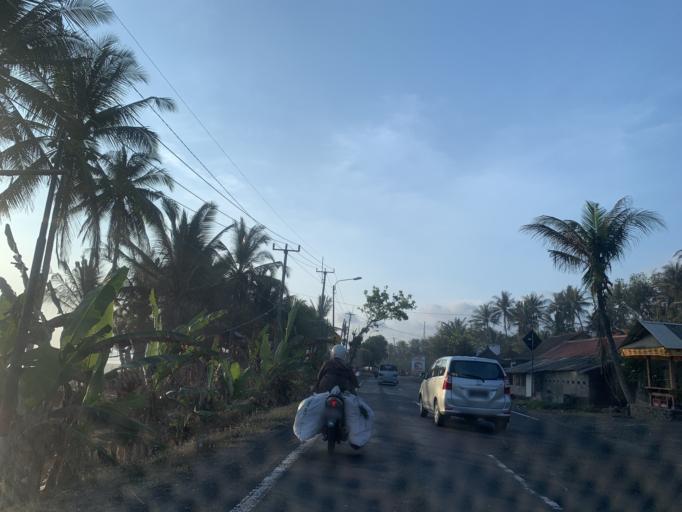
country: ID
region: Bali
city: Banjar Swastika
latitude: -8.4624
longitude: 114.9091
